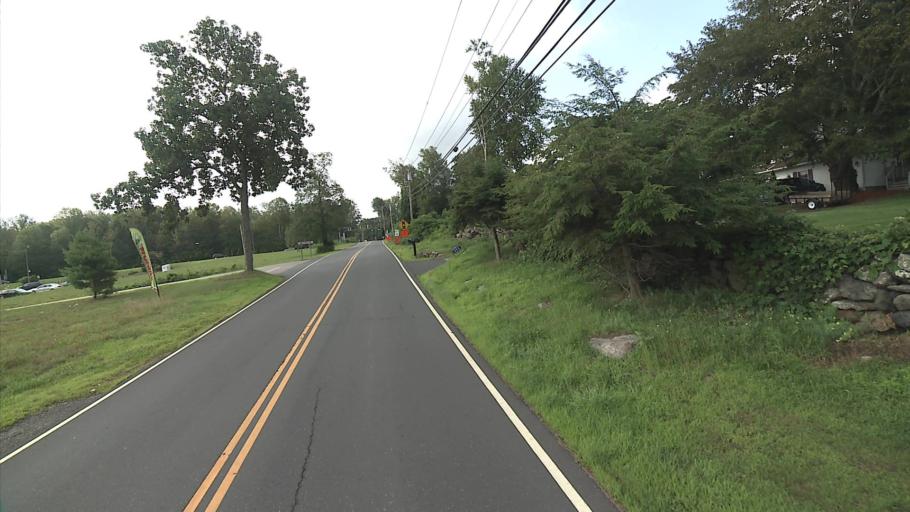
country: US
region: Connecticut
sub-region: Middlesex County
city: Moodus
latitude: 41.5471
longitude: -72.4129
